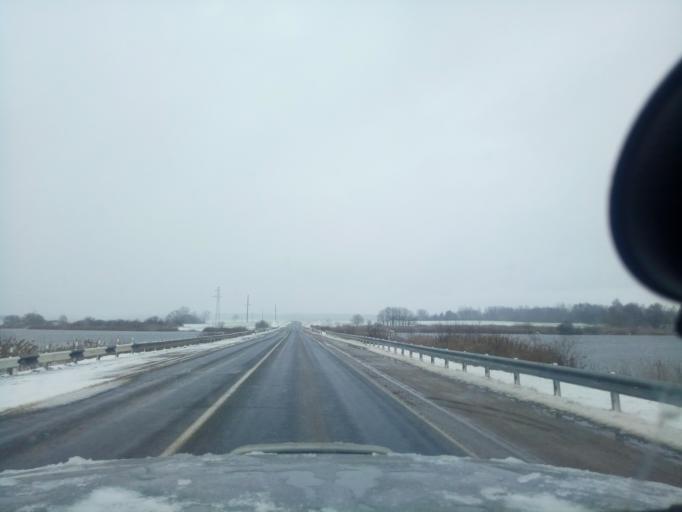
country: BY
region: Minsk
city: Nyasvizh
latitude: 53.2074
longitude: 26.6650
